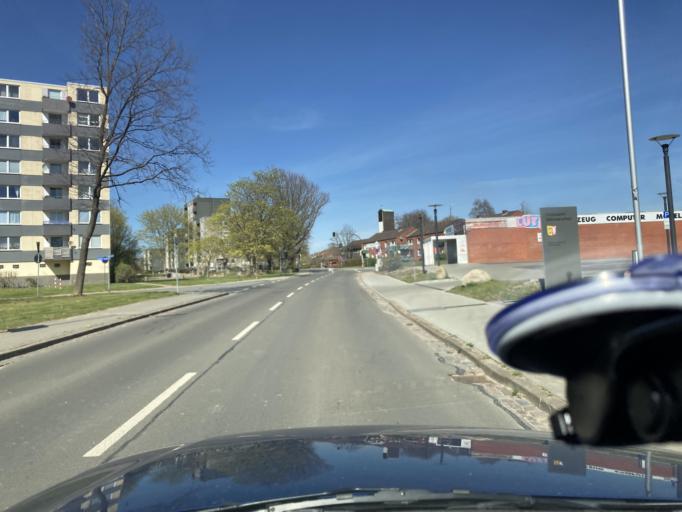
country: DE
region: Schleswig-Holstein
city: Heide
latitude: 54.1939
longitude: 9.1110
